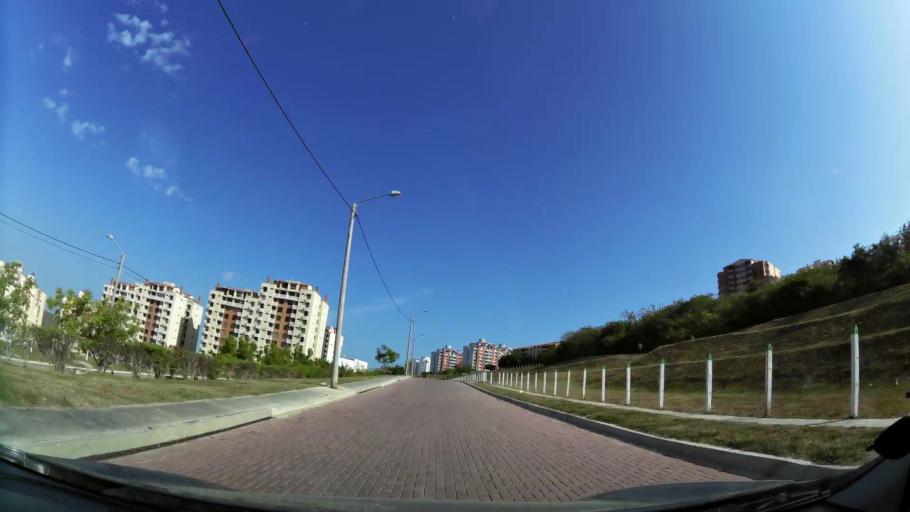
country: CO
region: Atlantico
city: Barranquilla
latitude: 10.9993
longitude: -74.8347
